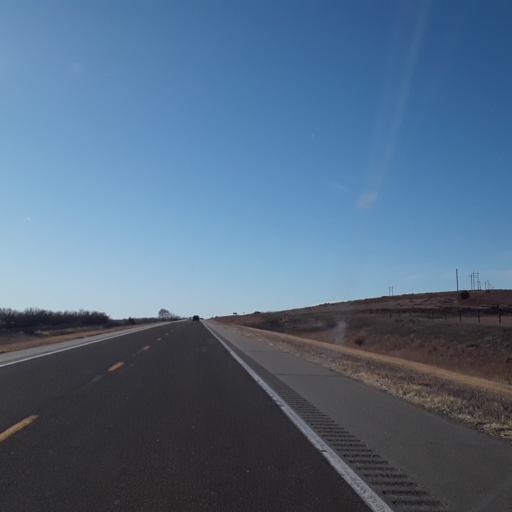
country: US
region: Nebraska
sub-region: Hitchcock County
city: Trenton
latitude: 40.1577
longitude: -101.1755
